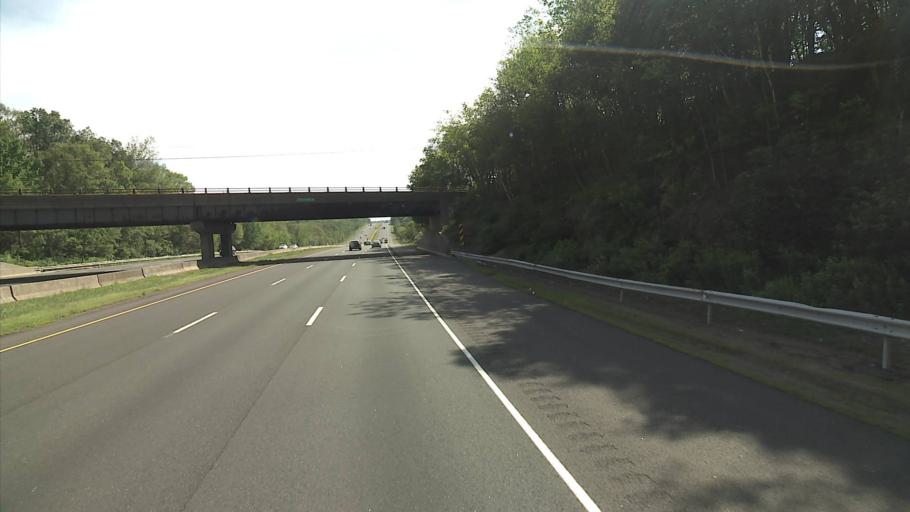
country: US
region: Connecticut
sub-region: Tolland County
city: Stafford Springs
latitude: 41.9382
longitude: -72.2297
